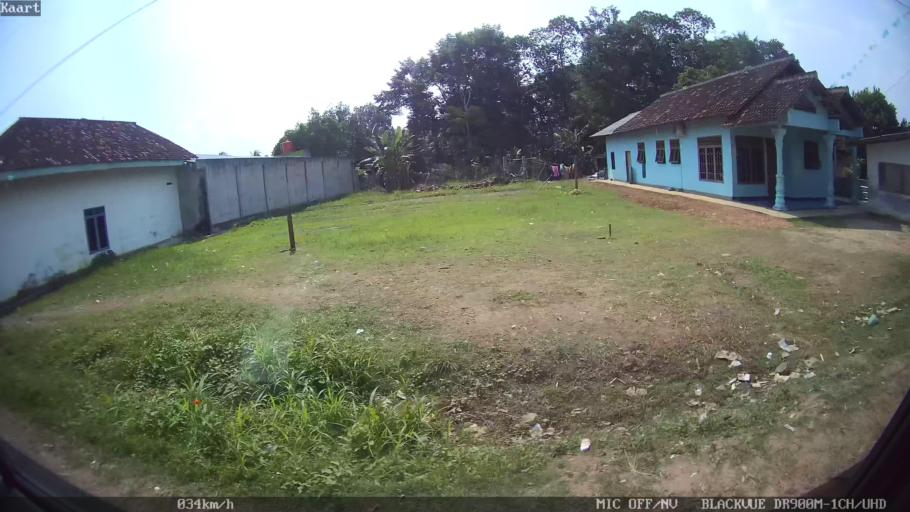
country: ID
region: Lampung
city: Natar
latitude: -5.2961
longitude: 105.2445
